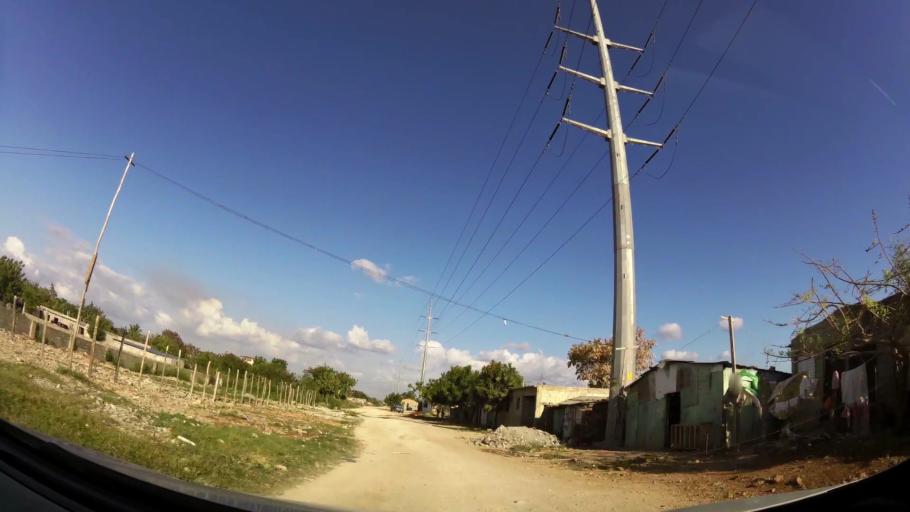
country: DO
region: Santo Domingo
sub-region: Santo Domingo
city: Santo Domingo Este
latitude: 18.4759
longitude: -69.8128
